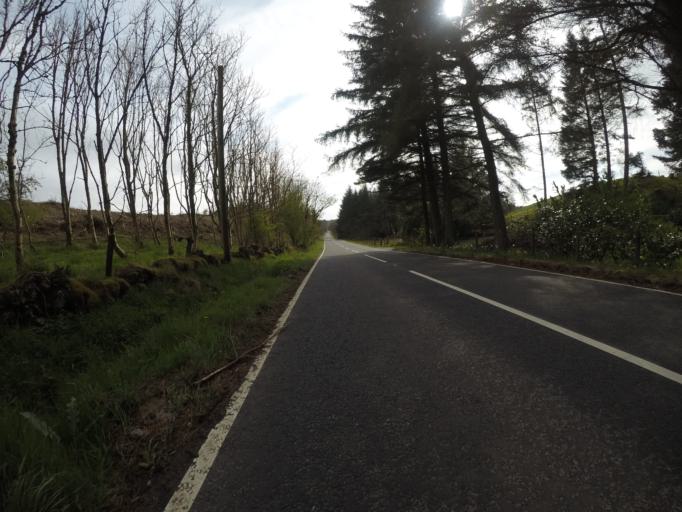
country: GB
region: Scotland
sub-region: East Renfrewshire
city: Newton Mearns
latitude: 55.7489
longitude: -4.3576
